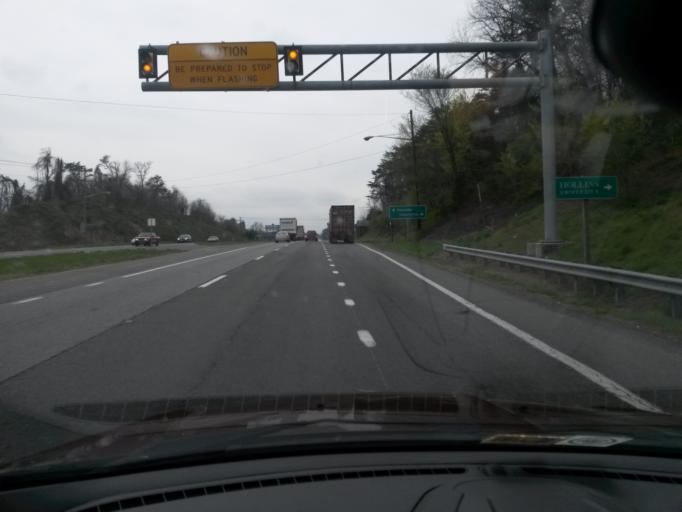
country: US
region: Virginia
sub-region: Botetourt County
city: Laymantown
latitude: 37.3274
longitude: -79.8672
